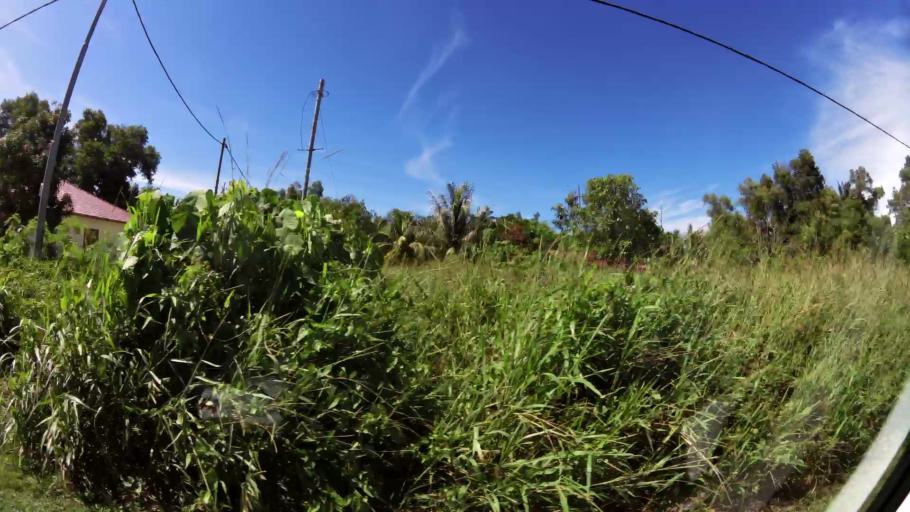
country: BN
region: Brunei and Muara
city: Bandar Seri Begawan
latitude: 5.0037
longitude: 115.0608
